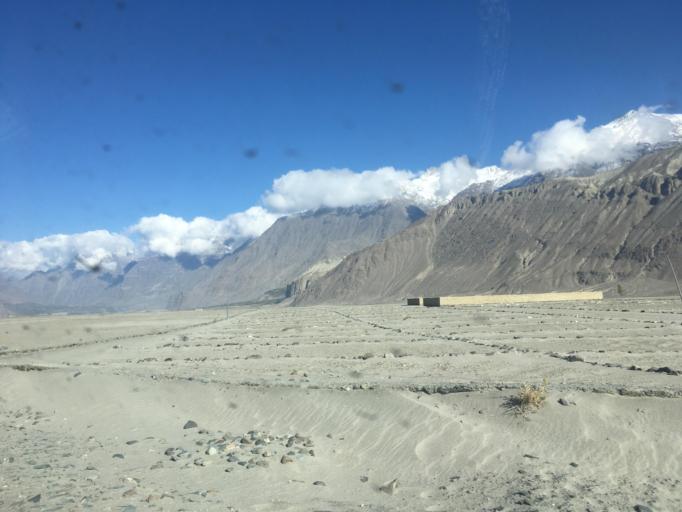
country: PK
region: Gilgit-Baltistan
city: Skardu
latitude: 35.3576
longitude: 75.5423
